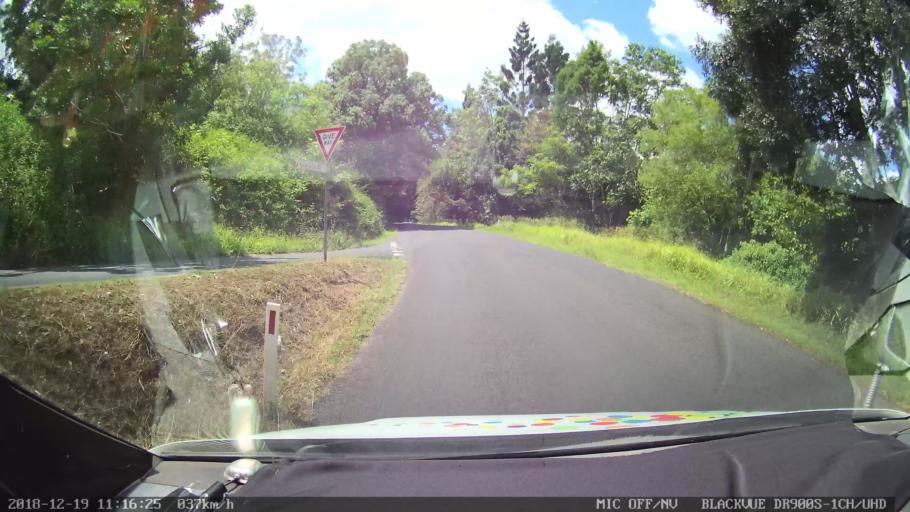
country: AU
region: New South Wales
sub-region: Lismore Municipality
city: Nimbin
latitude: -28.6739
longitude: 153.2779
